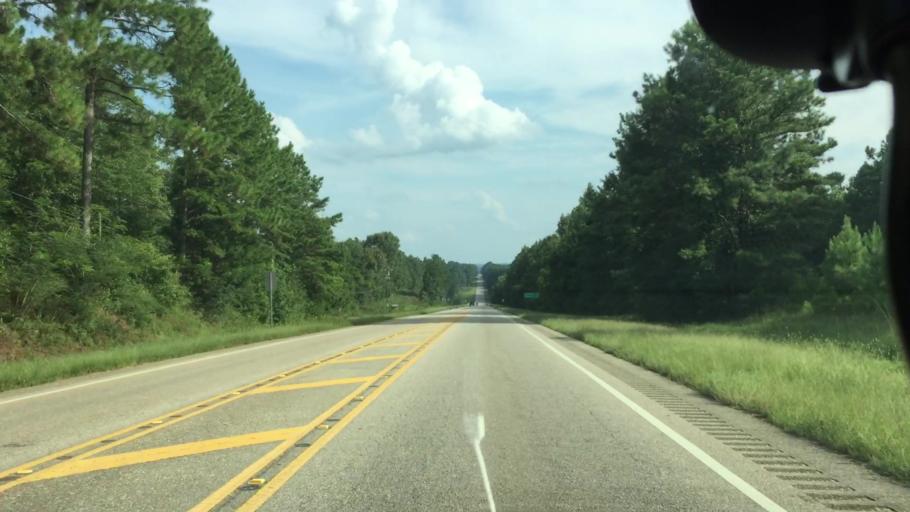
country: US
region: Alabama
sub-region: Pike County
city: Troy
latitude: 31.6749
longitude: -85.9565
